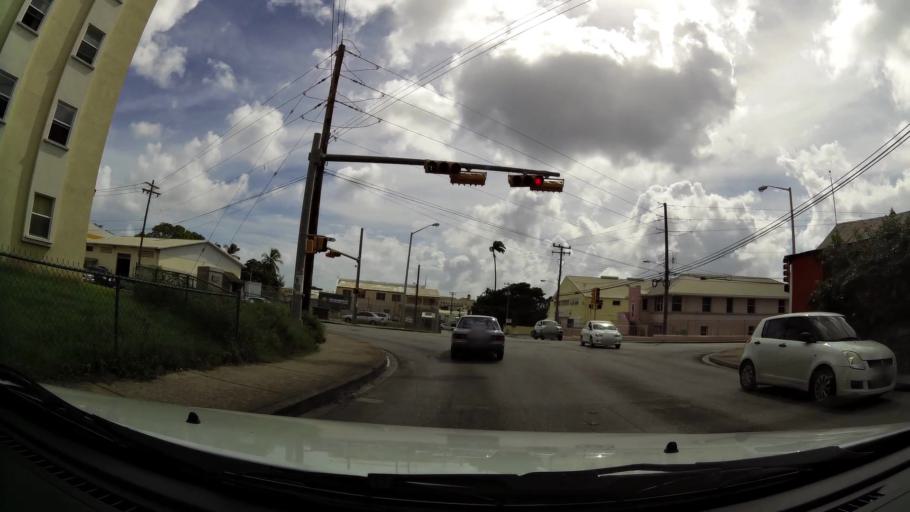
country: BB
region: Saint Michael
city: Bridgetown
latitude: 13.1062
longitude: -59.6131
